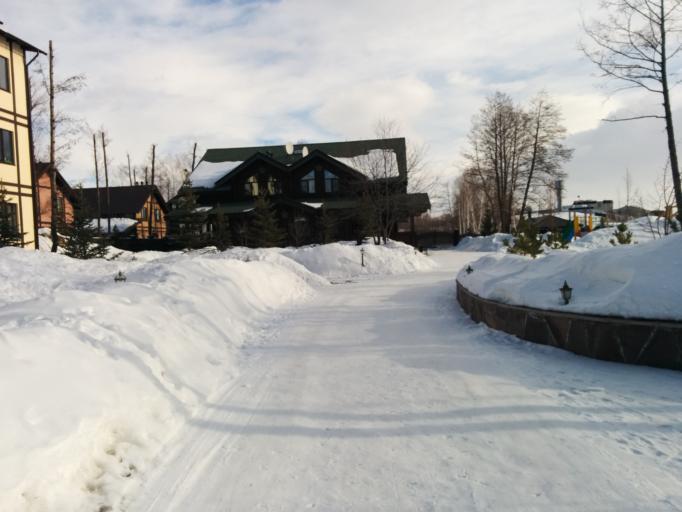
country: RU
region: Bashkortostan
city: Abzakovo
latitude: 53.5955
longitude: 58.6065
